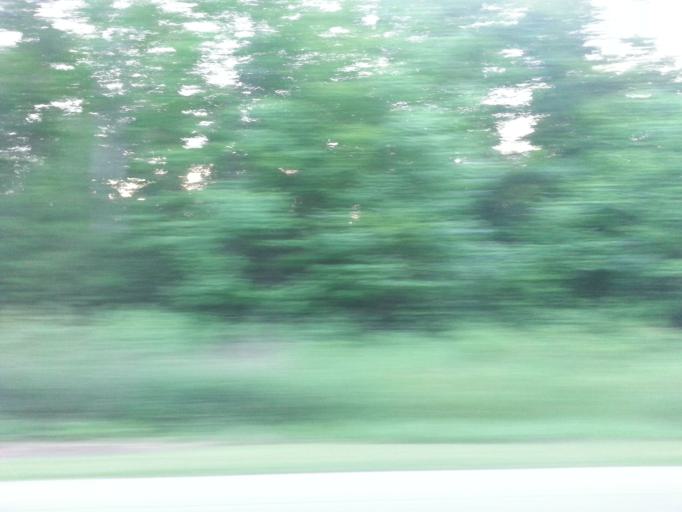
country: US
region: Tennessee
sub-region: McMinn County
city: Etowah
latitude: 35.2694
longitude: -84.2838
